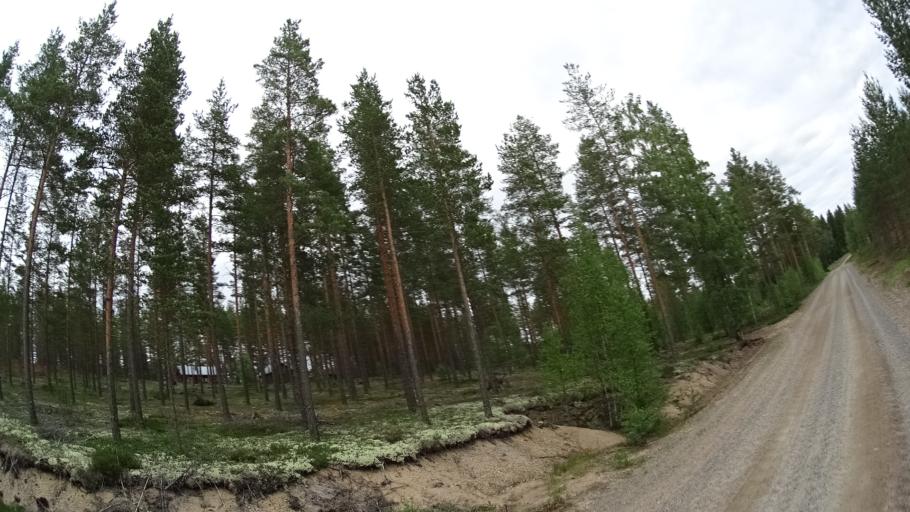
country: FI
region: Satakunta
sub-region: Pohjois-Satakunta
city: Jaemijaervi
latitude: 61.7686
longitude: 22.8230
